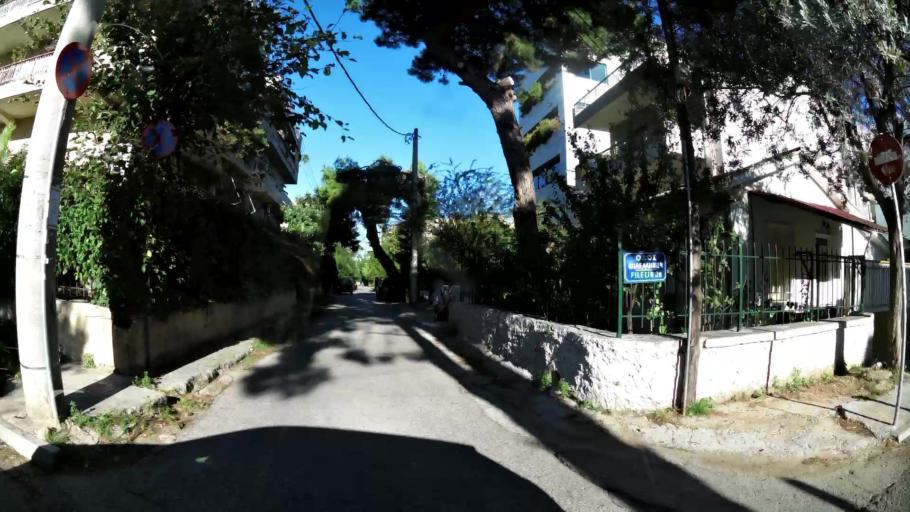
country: GR
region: Attica
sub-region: Nomarchia Athinas
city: Khalandrion
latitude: 38.0213
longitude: 23.7920
